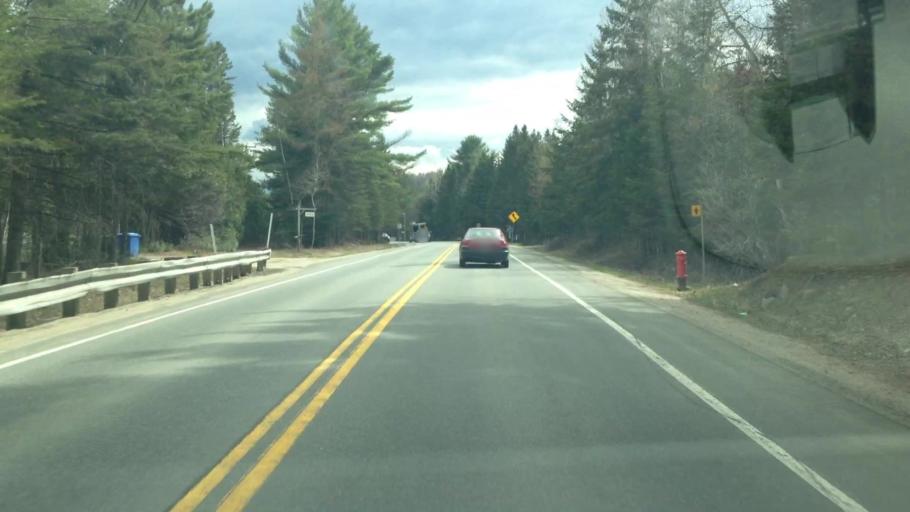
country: CA
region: Quebec
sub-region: Laurentides
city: Sainte-Adele
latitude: 46.0067
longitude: -74.1080
